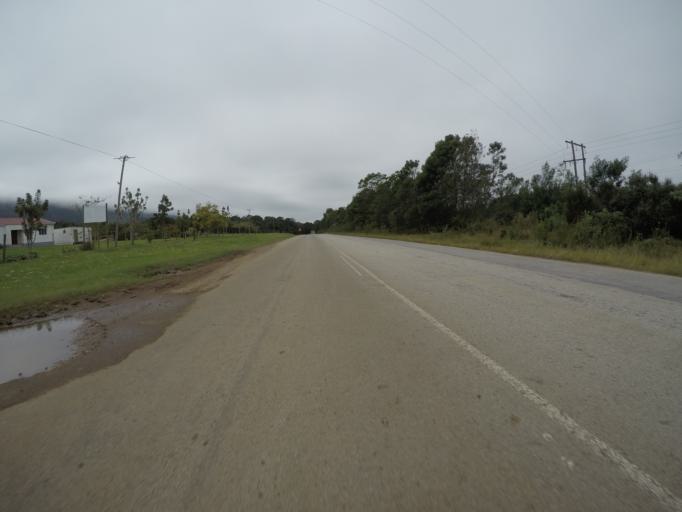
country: ZA
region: Eastern Cape
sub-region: Cacadu District Municipality
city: Kareedouw
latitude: -33.9974
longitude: 24.1653
